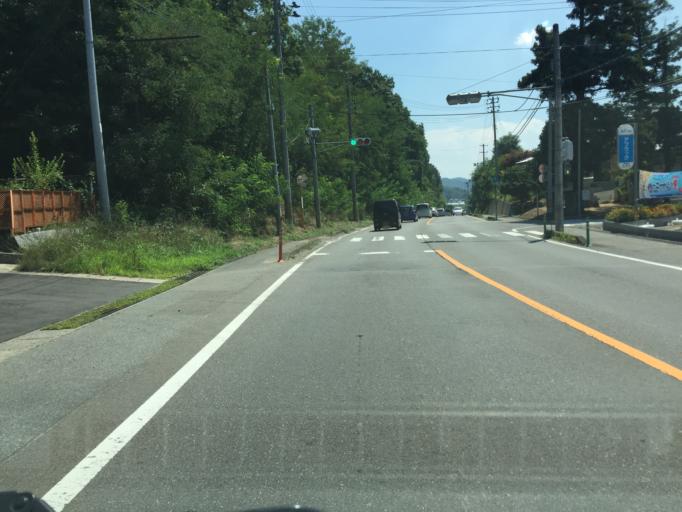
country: JP
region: Fukushima
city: Hobaramachi
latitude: 37.7971
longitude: 140.5176
